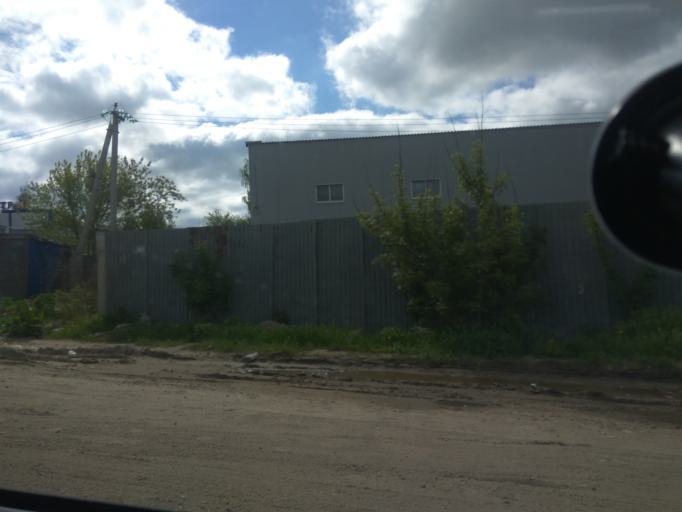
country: RU
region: Moskovskaya
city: Ostrovtsy
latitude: 55.5385
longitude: 38.0262
